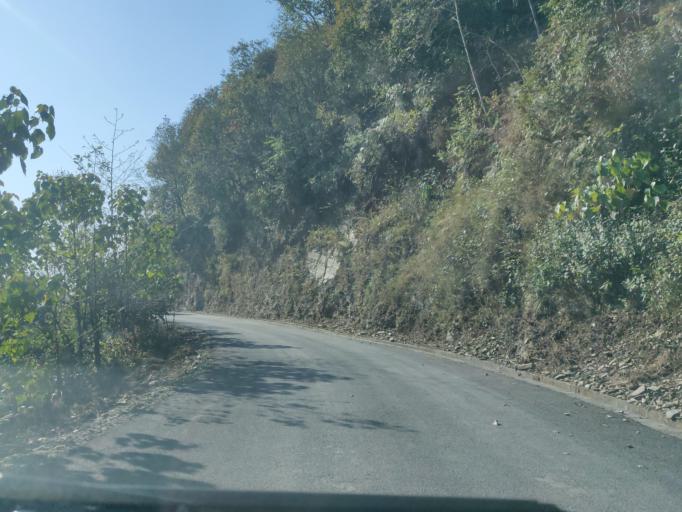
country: NP
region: Western Region
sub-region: Gandaki Zone
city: Pokhara
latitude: 28.2427
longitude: 83.9627
